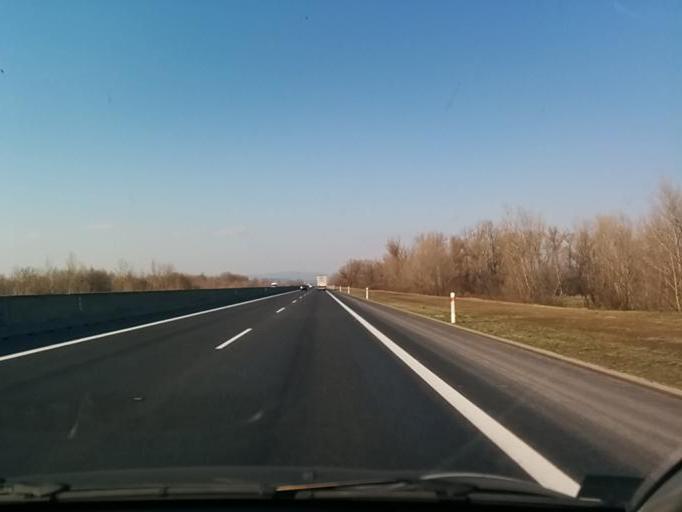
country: SK
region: Trenciansky
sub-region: Okres Nove Mesto nad Vahom
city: Nove Mesto nad Vahom
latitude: 48.6879
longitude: 17.8725
